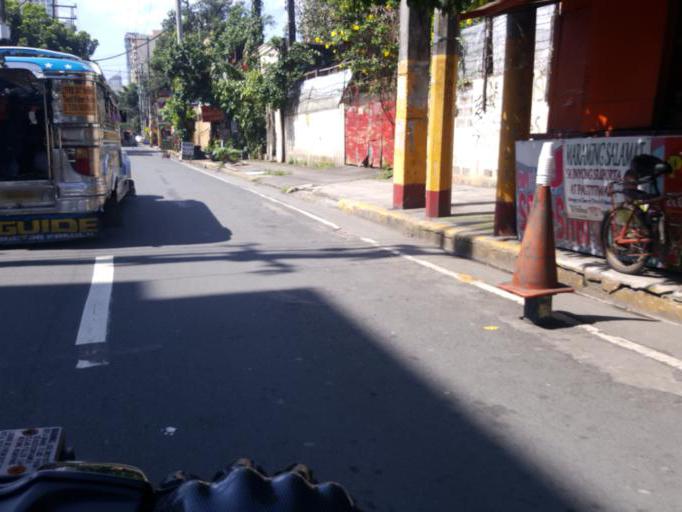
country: PH
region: Metro Manila
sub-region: City of Manila
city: Port Area
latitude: 14.5675
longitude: 120.9857
